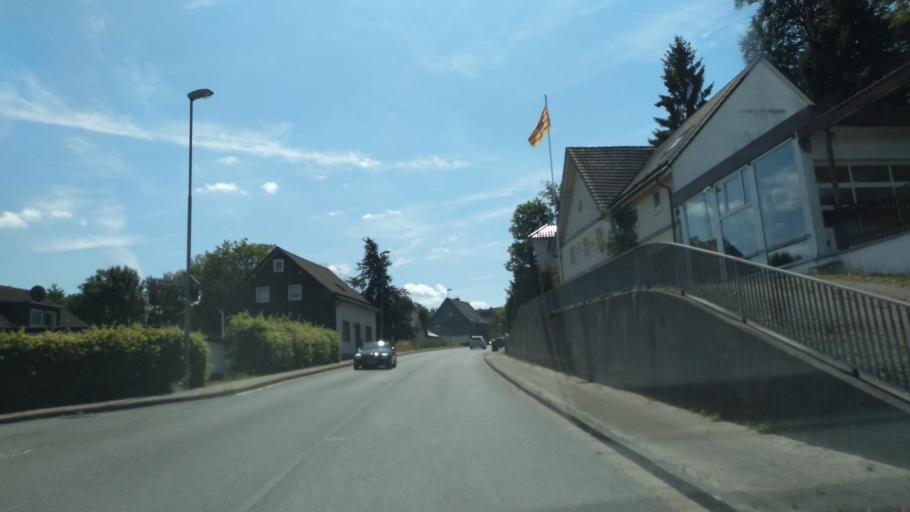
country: DE
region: North Rhine-Westphalia
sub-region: Regierungsbezirk Arnsberg
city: Olpe
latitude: 51.0524
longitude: 7.8585
